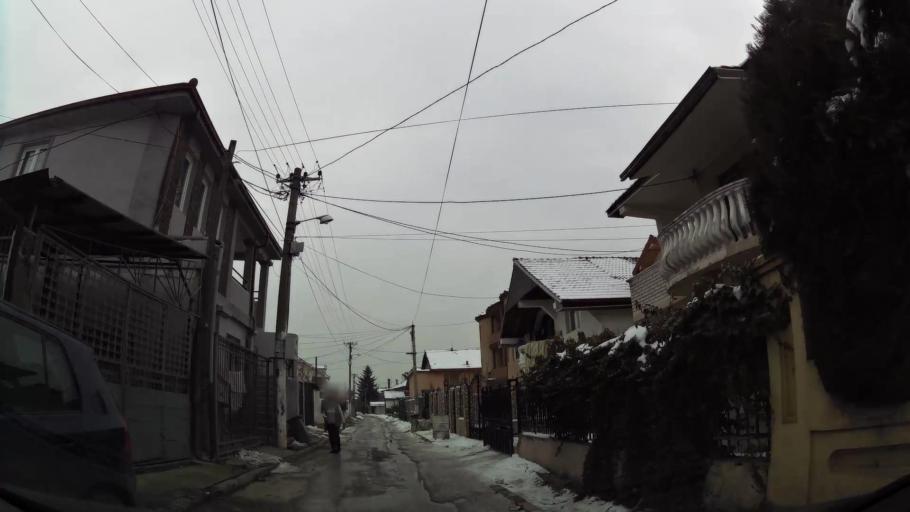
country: MK
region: Suto Orizari
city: Suto Orizare
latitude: 42.0350
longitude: 21.4235
